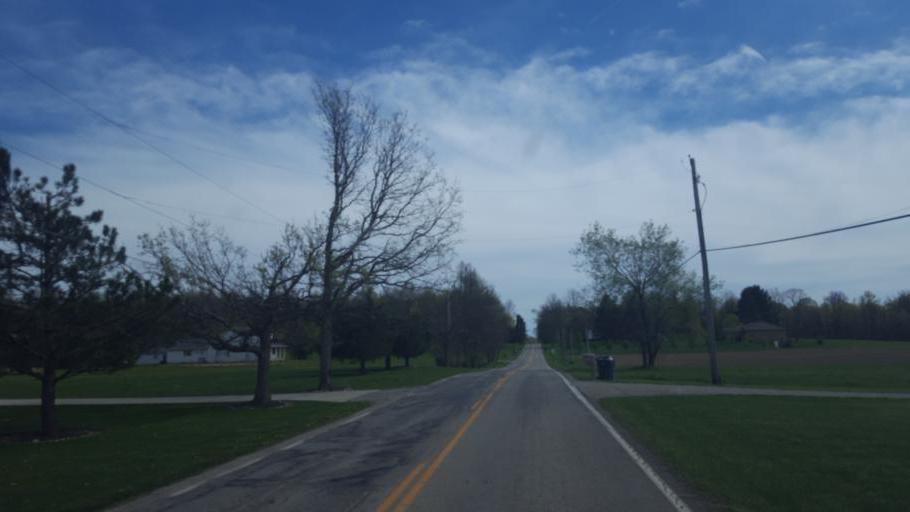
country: US
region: Ohio
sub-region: Richland County
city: Shelby
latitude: 40.8393
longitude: -82.6015
